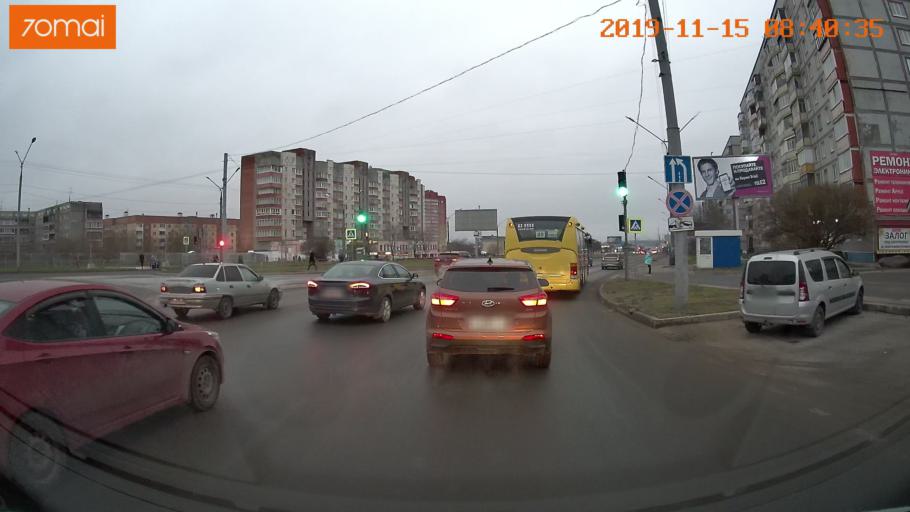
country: RU
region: Vologda
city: Cherepovets
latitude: 59.0949
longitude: 37.9140
